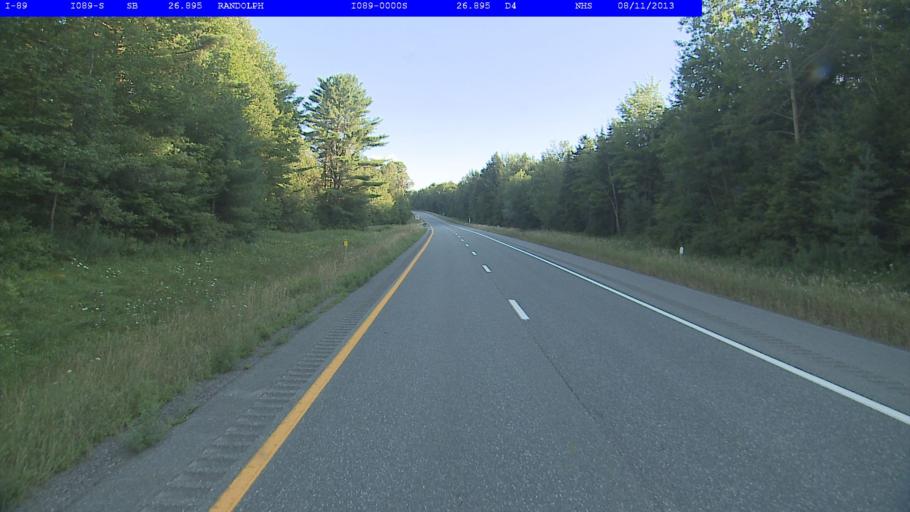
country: US
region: Vermont
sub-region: Orange County
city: Randolph
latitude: 43.8881
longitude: -72.6178
